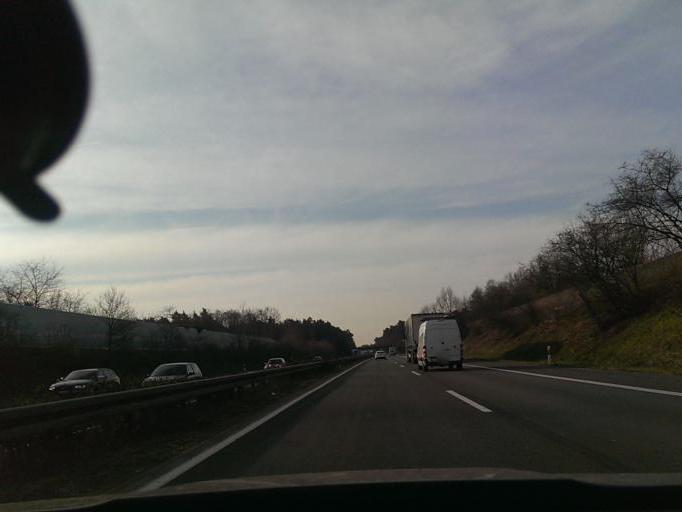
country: DE
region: North Rhine-Westphalia
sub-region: Regierungsbezirk Detmold
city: Oerlinghausen
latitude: 51.8921
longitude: 8.6402
